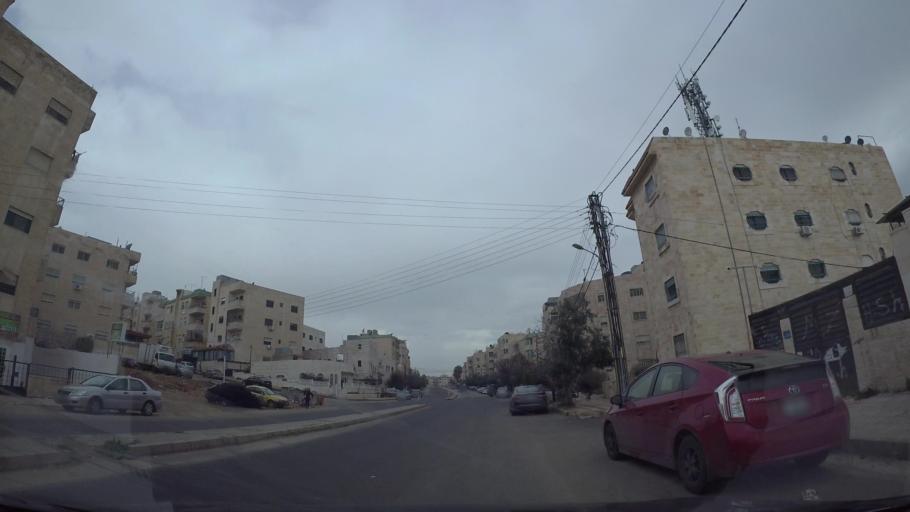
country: JO
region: Amman
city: Amman
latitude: 31.9828
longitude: 35.9309
